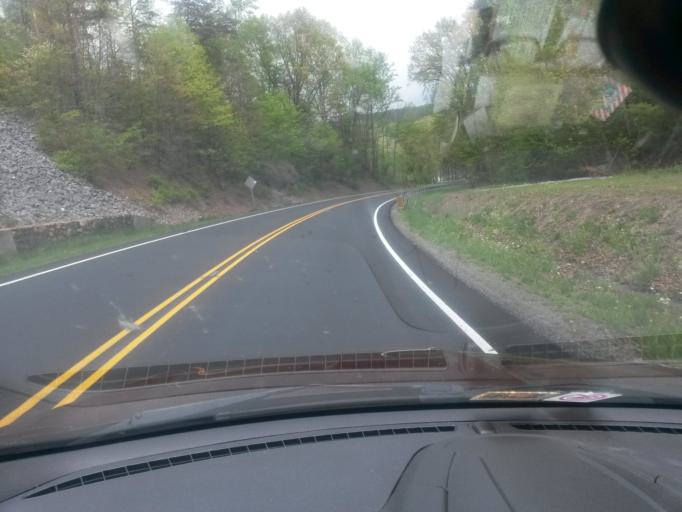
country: US
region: Virginia
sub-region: City of Covington
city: Covington
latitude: 37.8074
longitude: -80.0406
